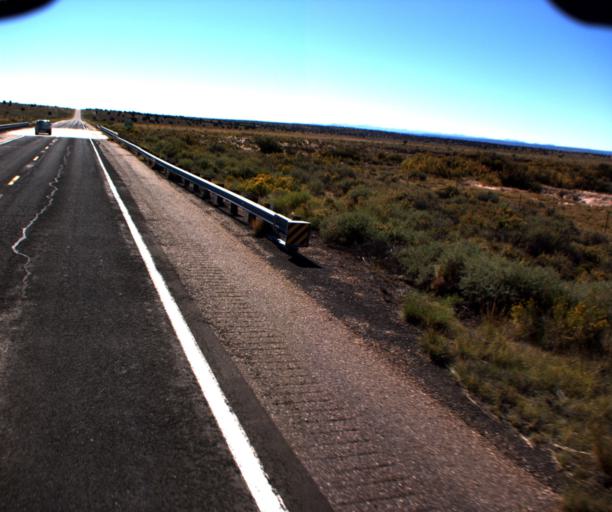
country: US
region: Arizona
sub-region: Navajo County
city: Snowflake
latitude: 34.6699
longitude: -109.7241
